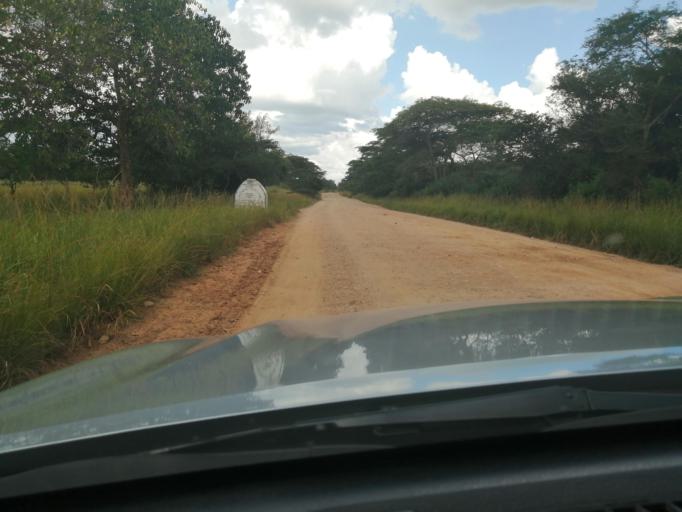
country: ZM
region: Lusaka
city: Lusaka
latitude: -15.2038
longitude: 28.0679
